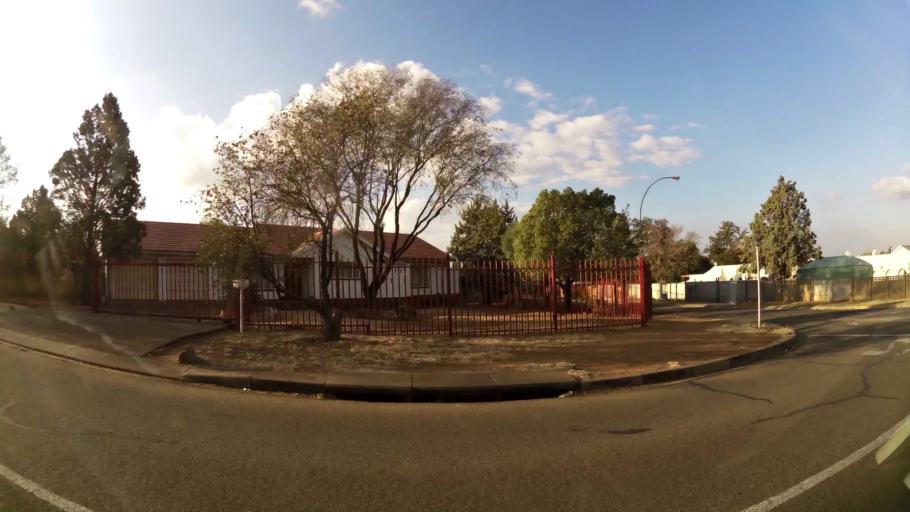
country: ZA
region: Orange Free State
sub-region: Mangaung Metropolitan Municipality
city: Bloemfontein
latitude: -29.1553
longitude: 26.1838
